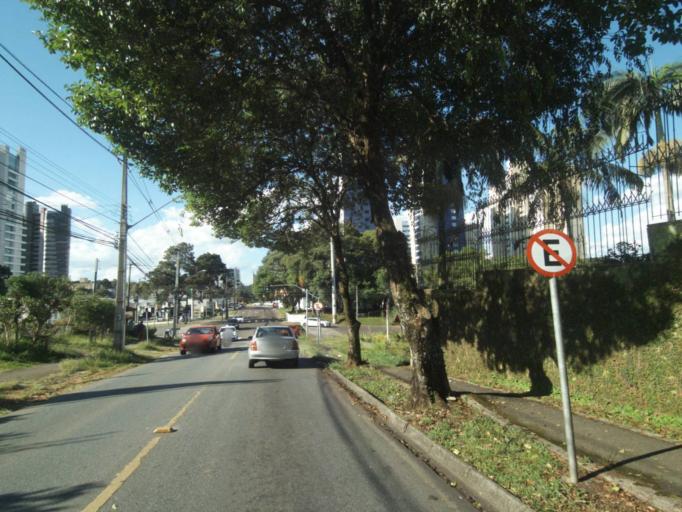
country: BR
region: Parana
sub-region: Curitiba
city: Curitiba
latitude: -25.4395
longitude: -49.3220
